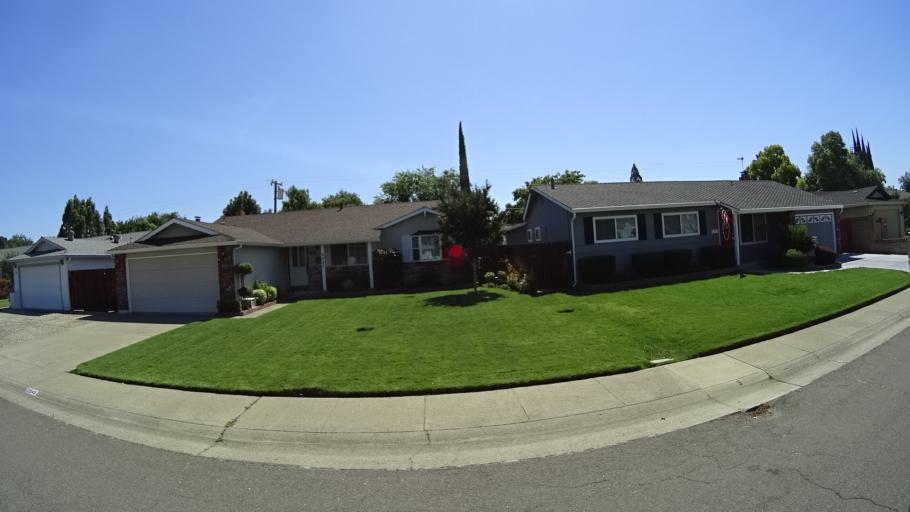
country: US
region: California
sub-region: Sacramento County
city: Rosemont
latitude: 38.5523
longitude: -121.3883
